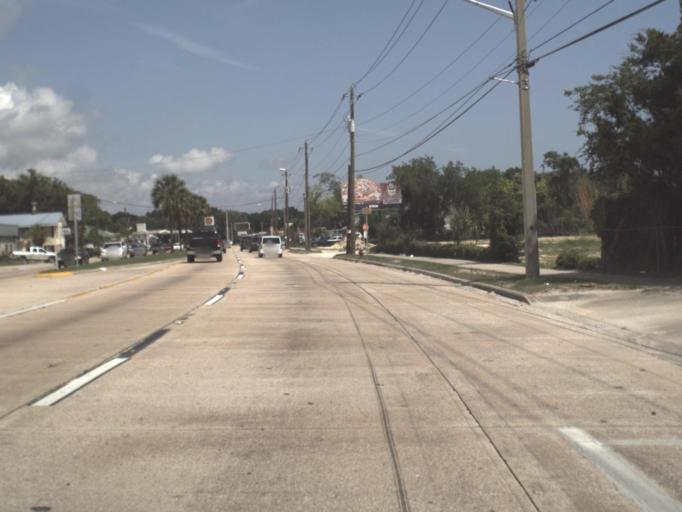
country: US
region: Florida
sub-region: Saint Johns County
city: Saint Augustine
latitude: 29.8878
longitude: -81.3238
